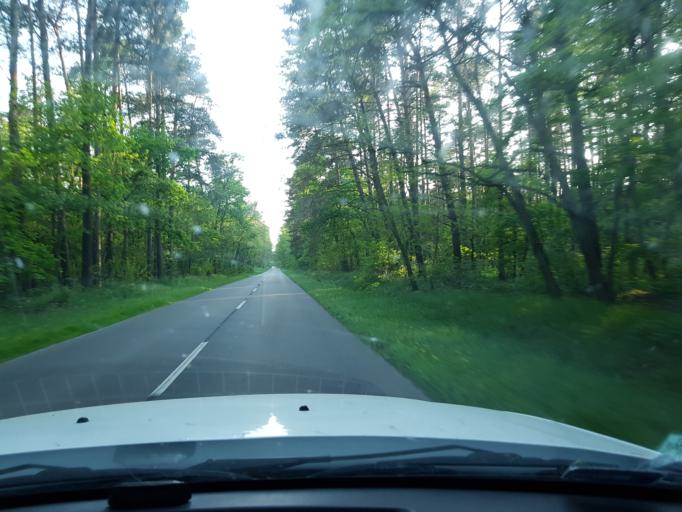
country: PL
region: West Pomeranian Voivodeship
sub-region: Powiat goleniowski
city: Mosty
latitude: 53.4454
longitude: 14.9243
